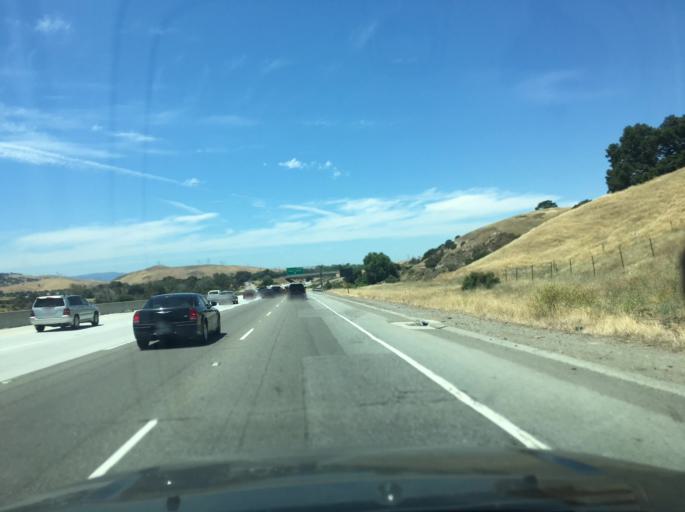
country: US
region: California
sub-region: Santa Clara County
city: Morgan Hill
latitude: 37.2052
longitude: -121.7154
